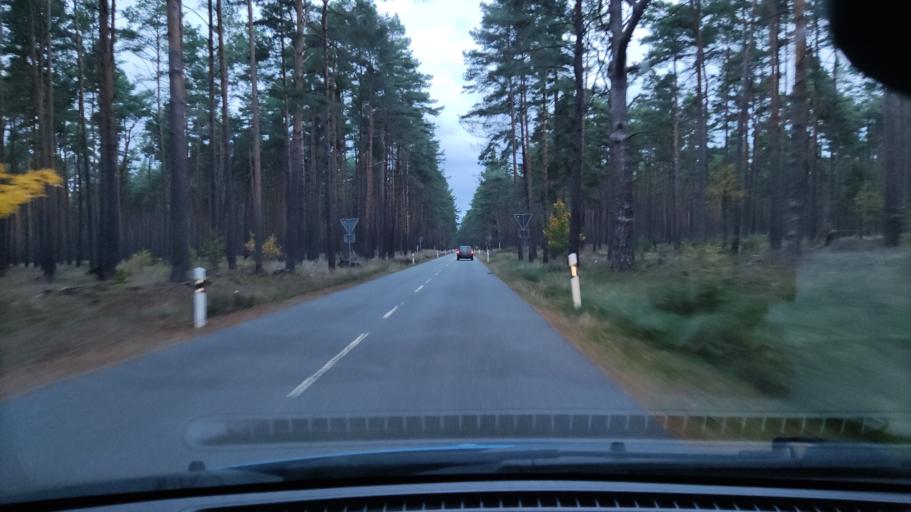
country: DE
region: Lower Saxony
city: Prezelle
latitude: 53.0122
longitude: 11.3892
